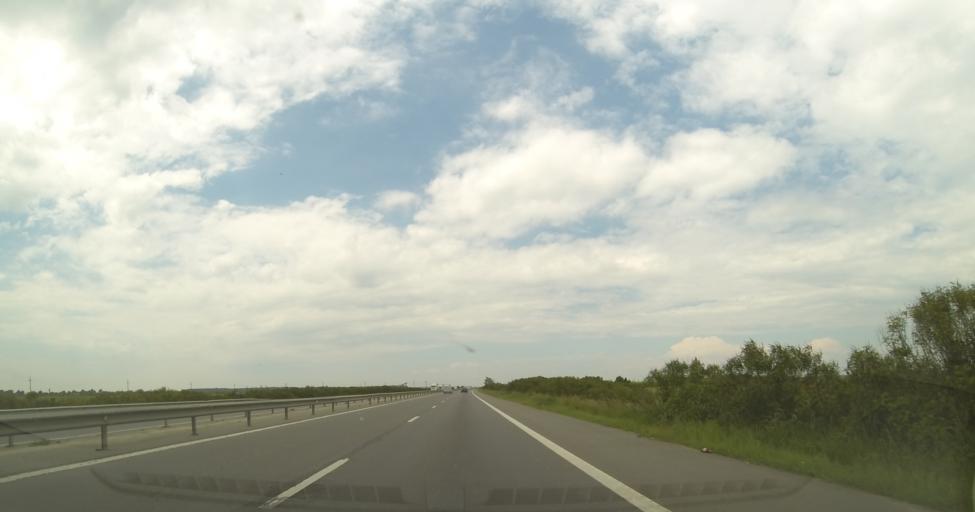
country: RO
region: Dambovita
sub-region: Comuna Corbii Mari
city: Corbii Mari
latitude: 44.5501
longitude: 25.5056
